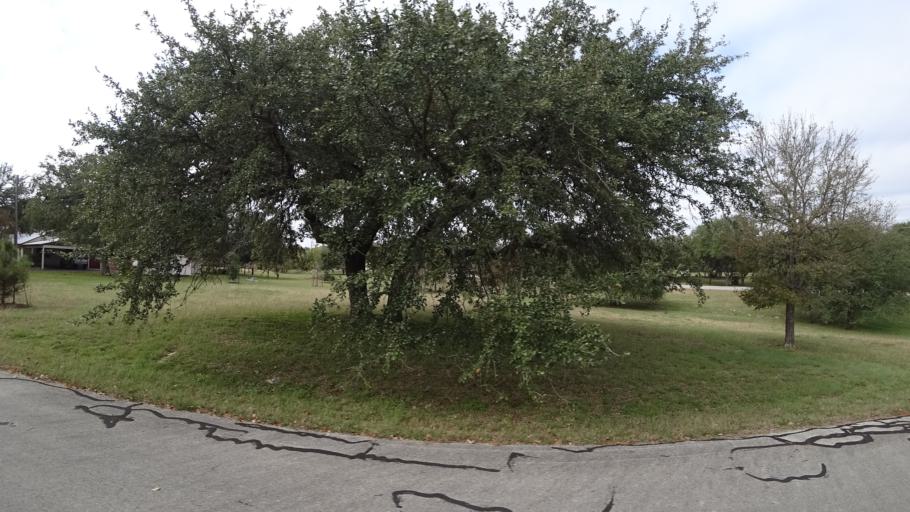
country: US
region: Texas
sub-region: Travis County
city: Shady Hollow
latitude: 30.1362
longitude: -97.8947
